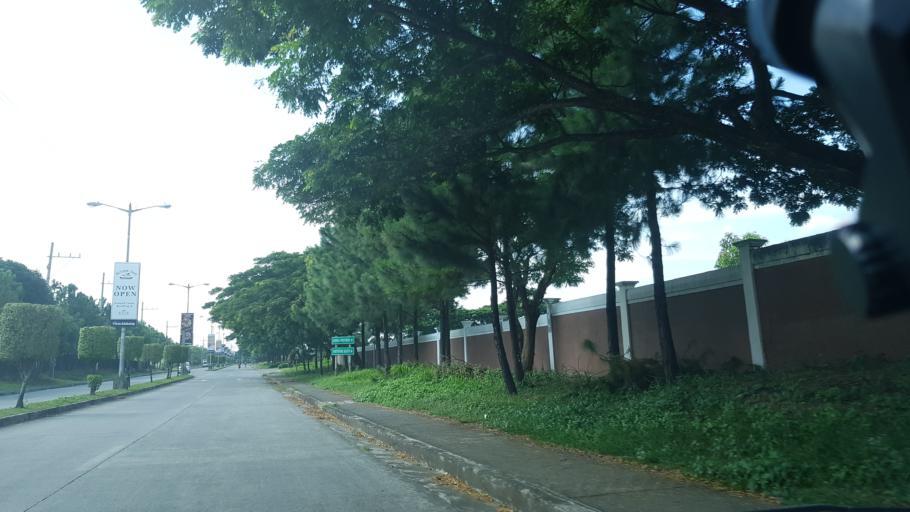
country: PH
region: Calabarzon
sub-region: Province of Laguna
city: Magsaysay
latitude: 14.3603
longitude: 121.0095
